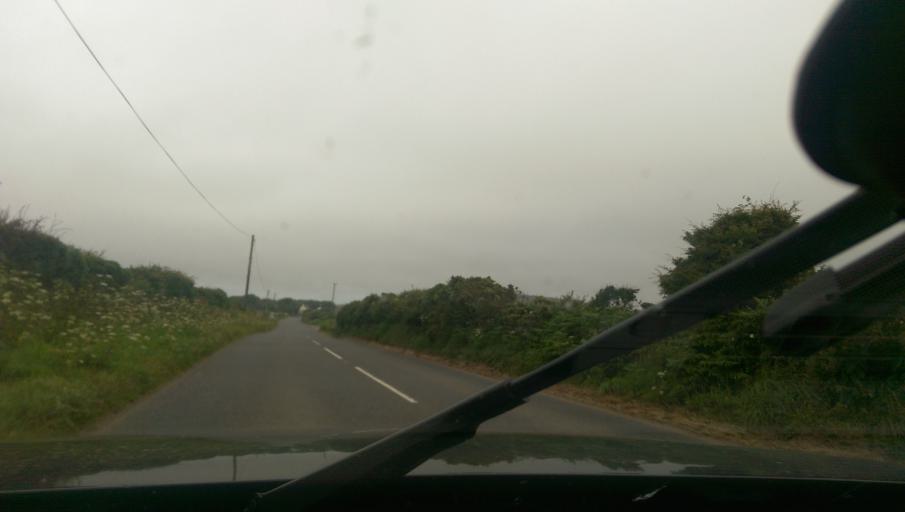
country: GB
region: England
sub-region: Cornwall
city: St. Buryan
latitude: 50.0912
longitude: -5.6374
